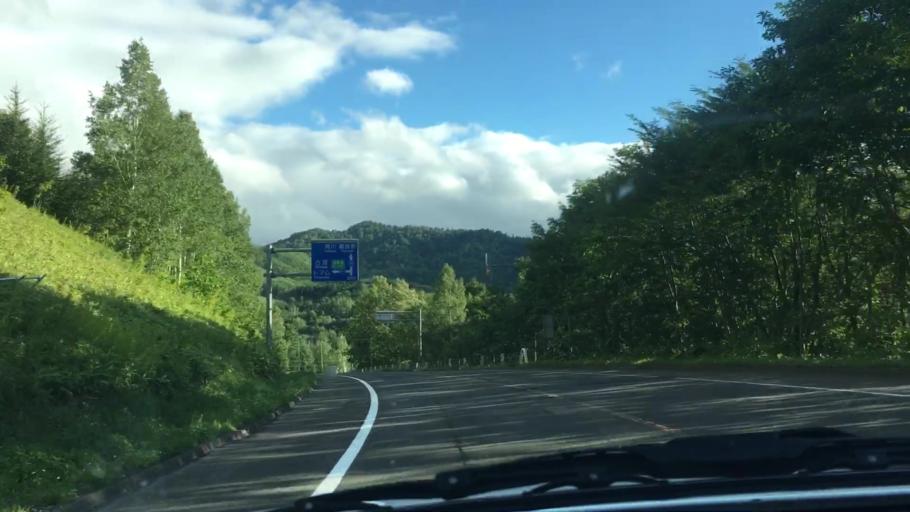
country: JP
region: Hokkaido
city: Shimo-furano
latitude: 43.1271
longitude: 142.6777
